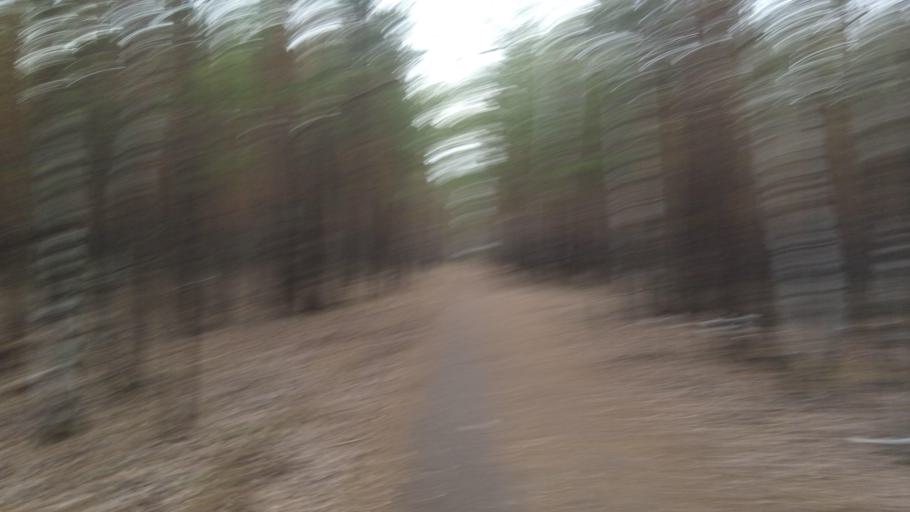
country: RU
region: Chelyabinsk
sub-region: Gorod Chelyabinsk
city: Chelyabinsk
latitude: 55.1329
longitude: 61.3430
